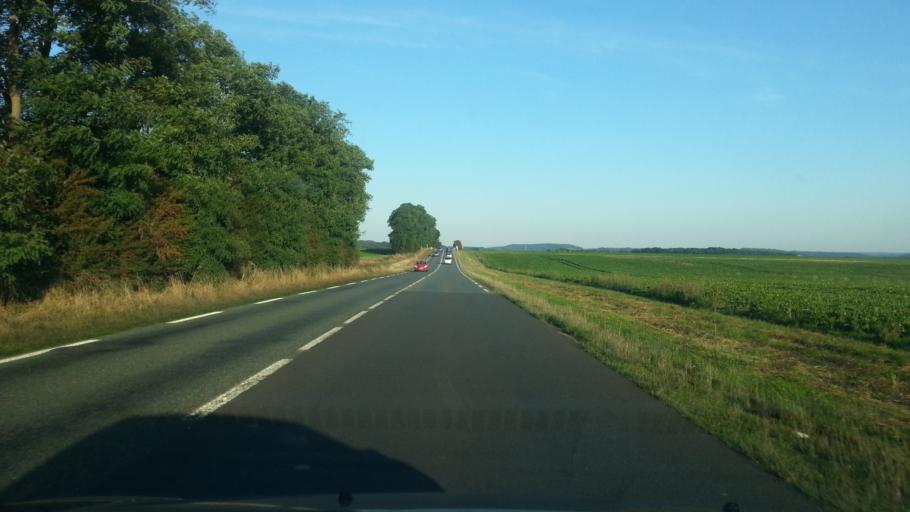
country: FR
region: Picardie
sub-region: Departement de l'Oise
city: Estrees-Saint-Denis
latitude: 49.4037
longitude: 2.6339
